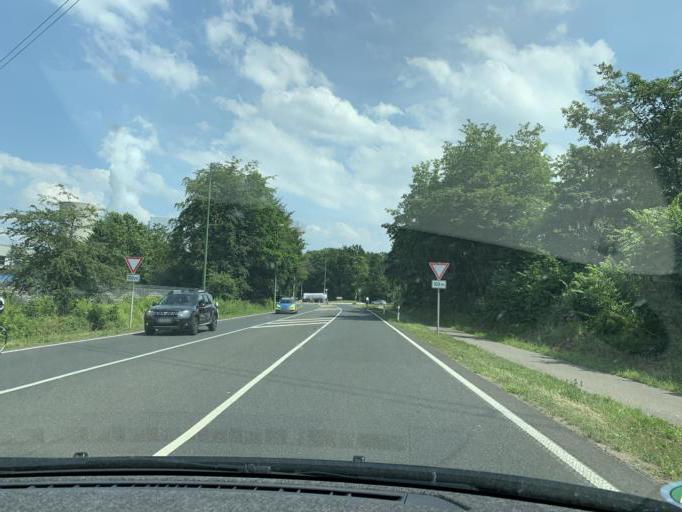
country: DE
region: North Rhine-Westphalia
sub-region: Regierungsbezirk Koln
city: Bedburg
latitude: 51.0350
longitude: 6.6134
